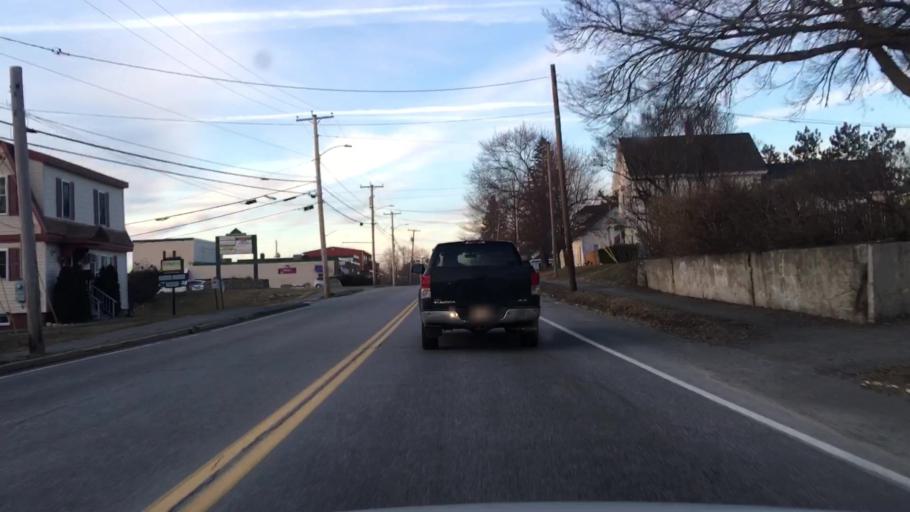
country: US
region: Maine
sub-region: Penobscot County
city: Brewer
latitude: 44.7900
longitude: -68.7561
